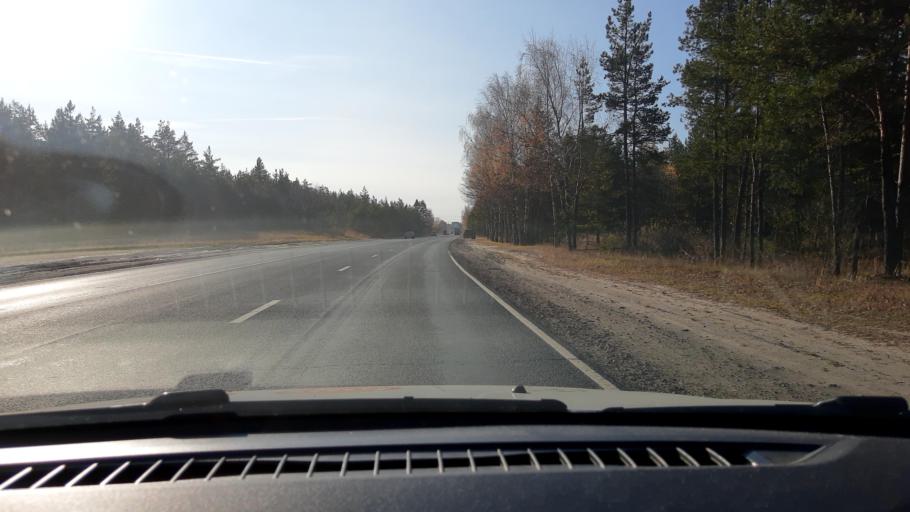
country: RU
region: Nizjnij Novgorod
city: Dzerzhinsk
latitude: 56.2732
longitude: 43.4742
